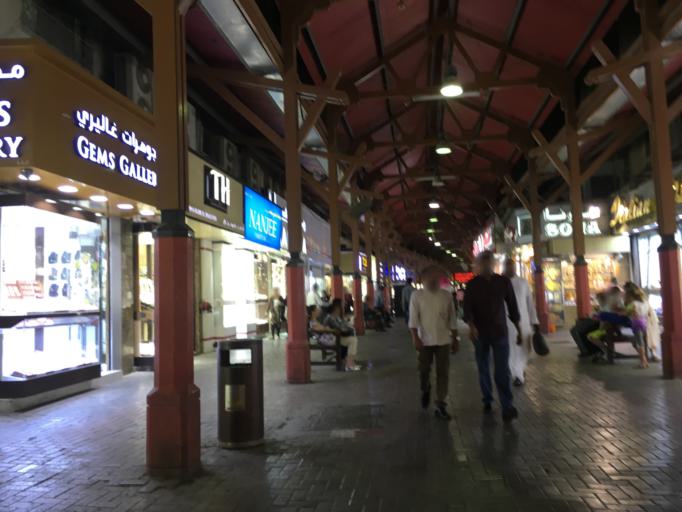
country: AE
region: Ash Shariqah
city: Sharjah
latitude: 25.2696
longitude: 55.2977
